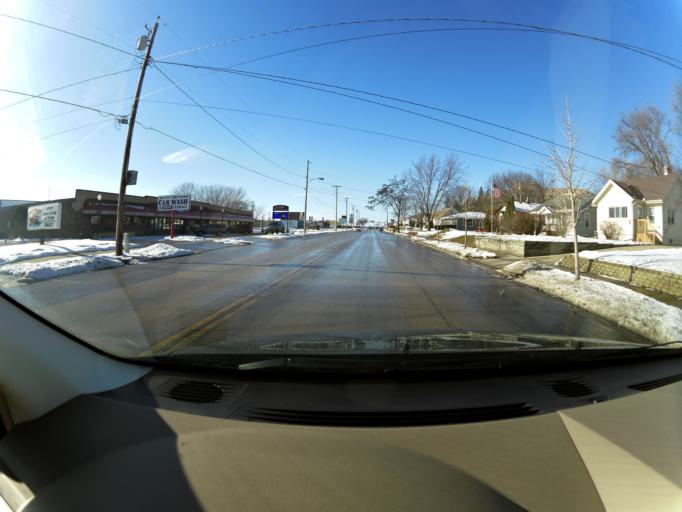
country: US
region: Minnesota
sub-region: Olmsted County
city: Rochester
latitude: 44.0311
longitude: -92.4751
